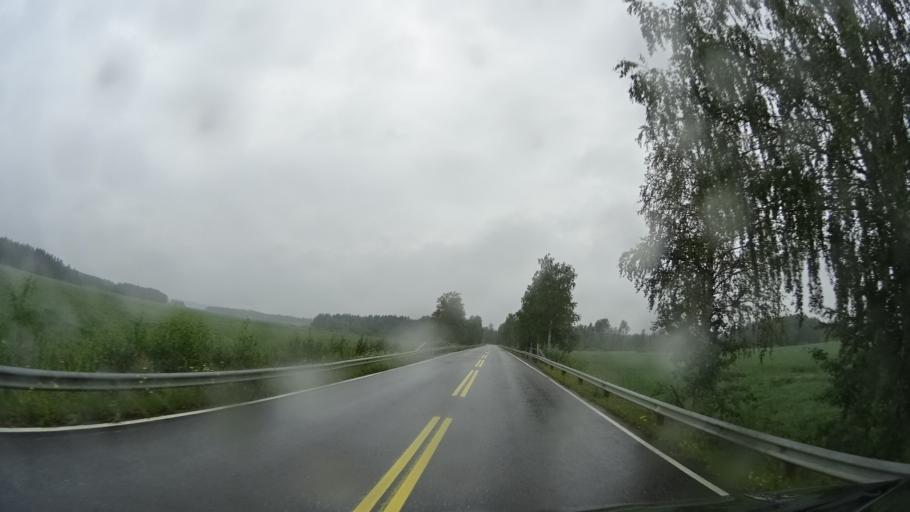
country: FI
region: North Karelia
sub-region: Keski-Karjala
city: Raeaekkylae
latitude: 62.3070
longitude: 29.5380
